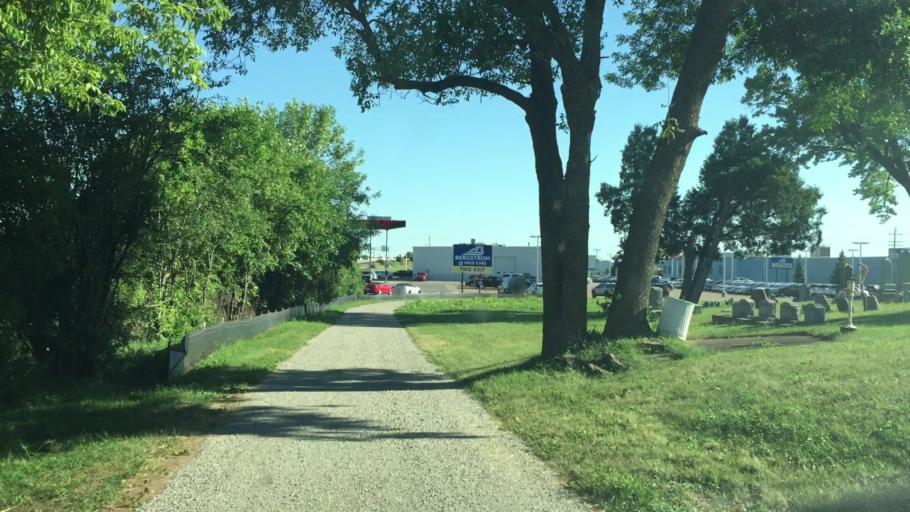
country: US
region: Wisconsin
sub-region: Winnebago County
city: Neenah
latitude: 44.1955
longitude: -88.4865
